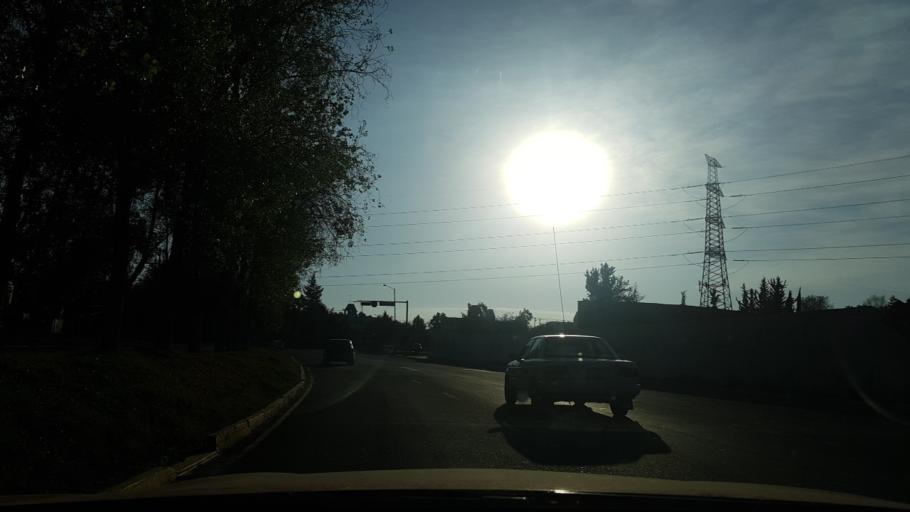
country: MX
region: Mexico
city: Cuautitlan Izcalli
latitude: 19.6475
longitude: -99.2248
